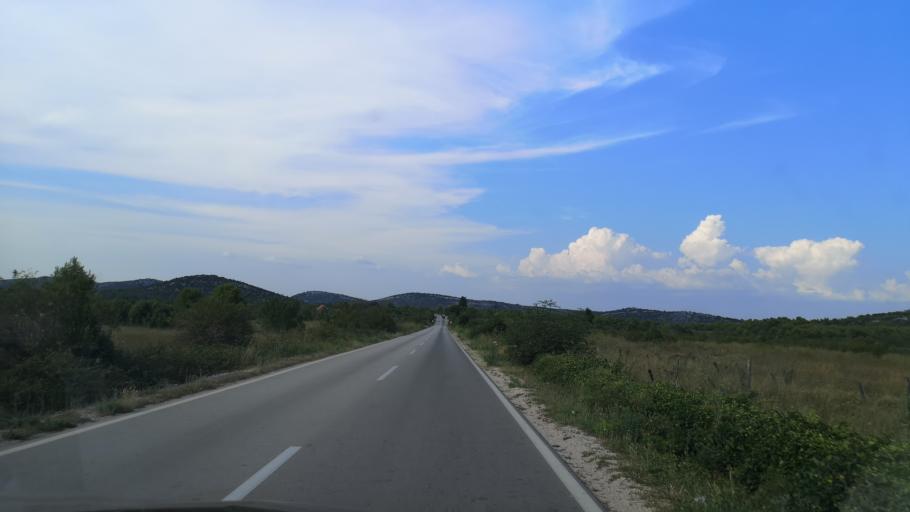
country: HR
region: Sibensko-Kniniska
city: Vodice
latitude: 43.8059
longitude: 15.7751
